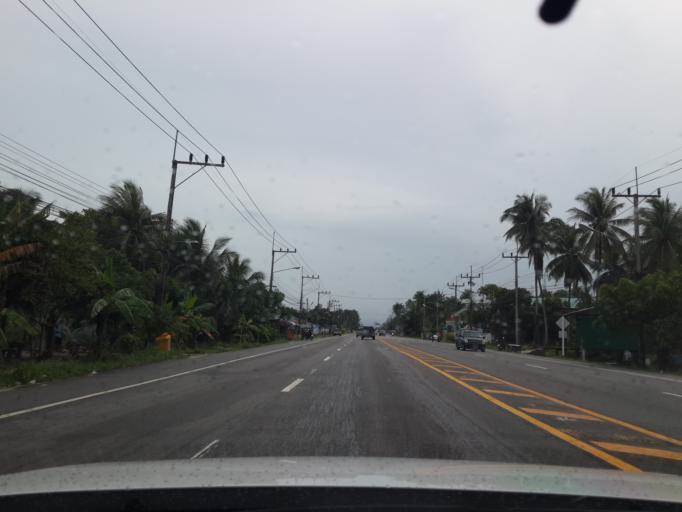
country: TH
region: Pattani
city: Nong Chik
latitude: 6.8497
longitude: 101.1947
